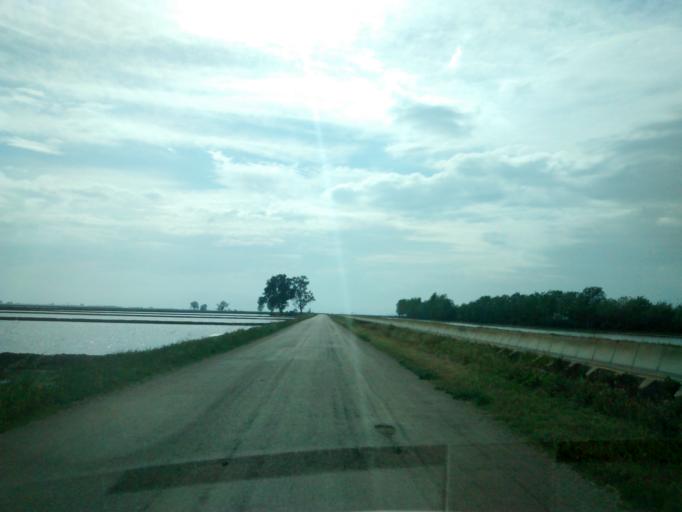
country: ES
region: Catalonia
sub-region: Provincia de Tarragona
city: Deltebre
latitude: 40.6932
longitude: 0.7968
